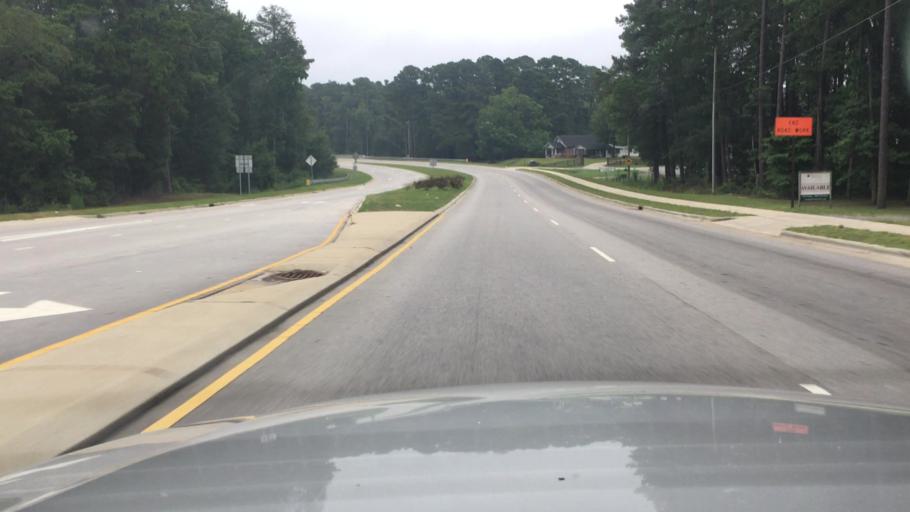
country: US
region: North Carolina
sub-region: Cumberland County
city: Hope Mills
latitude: 34.9859
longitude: -78.9632
